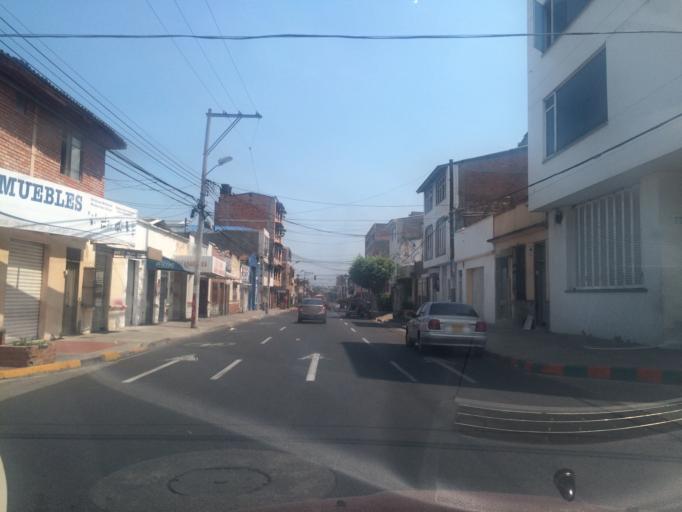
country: CO
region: Valle del Cauca
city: Cali
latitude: 3.4383
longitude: -76.5350
